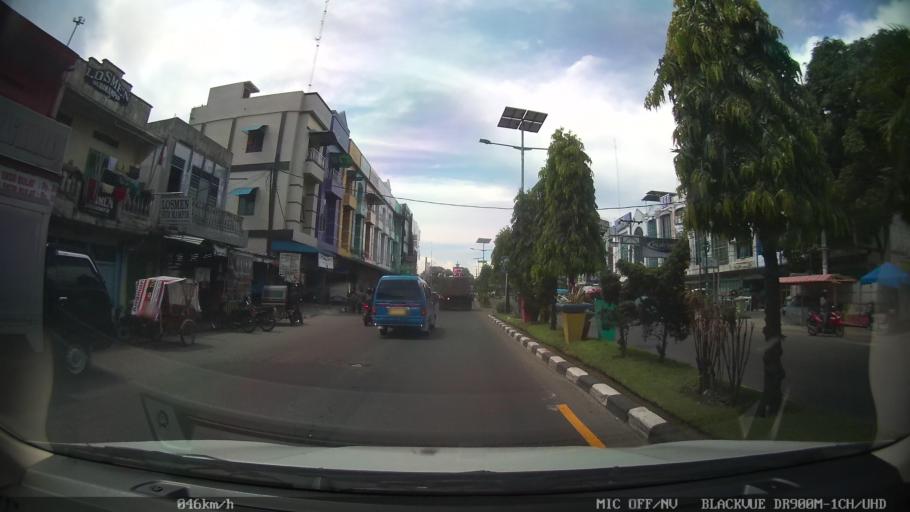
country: ID
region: North Sumatra
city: Binjai
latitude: 3.6138
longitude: 98.4965
